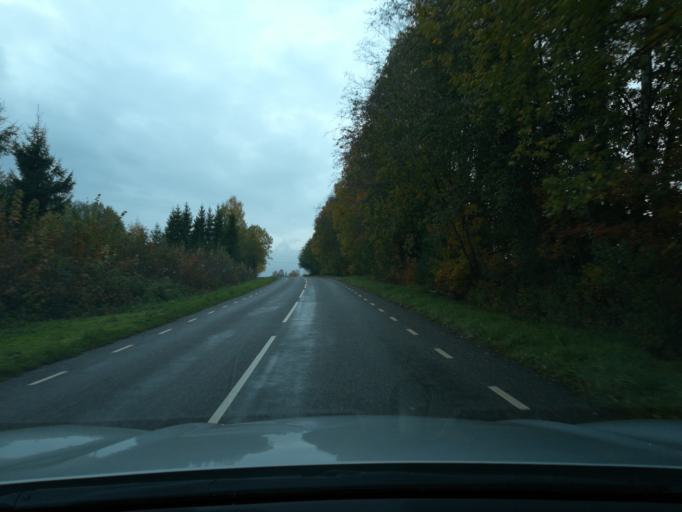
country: EE
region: Ida-Virumaa
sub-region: Johvi vald
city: Johvi
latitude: 59.0730
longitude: 27.3692
